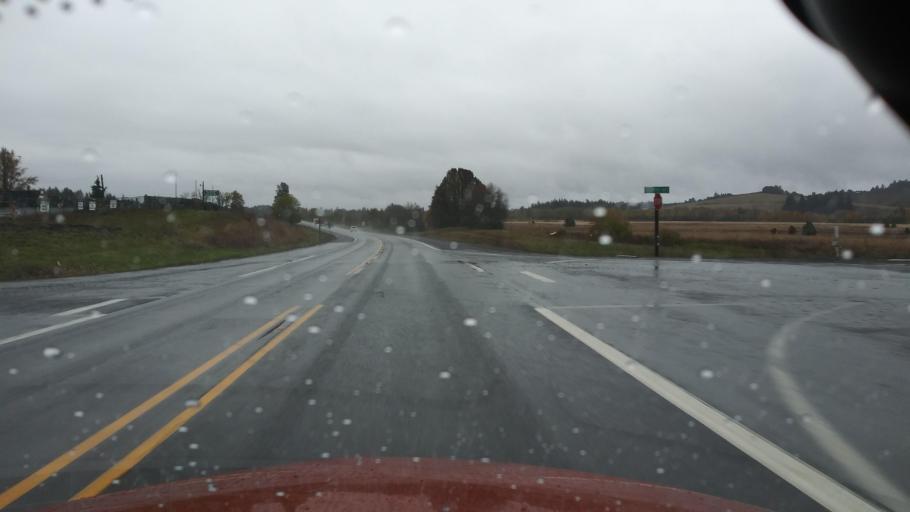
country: US
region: Oregon
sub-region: Washington County
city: Forest Grove
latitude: 45.4626
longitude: -123.1397
